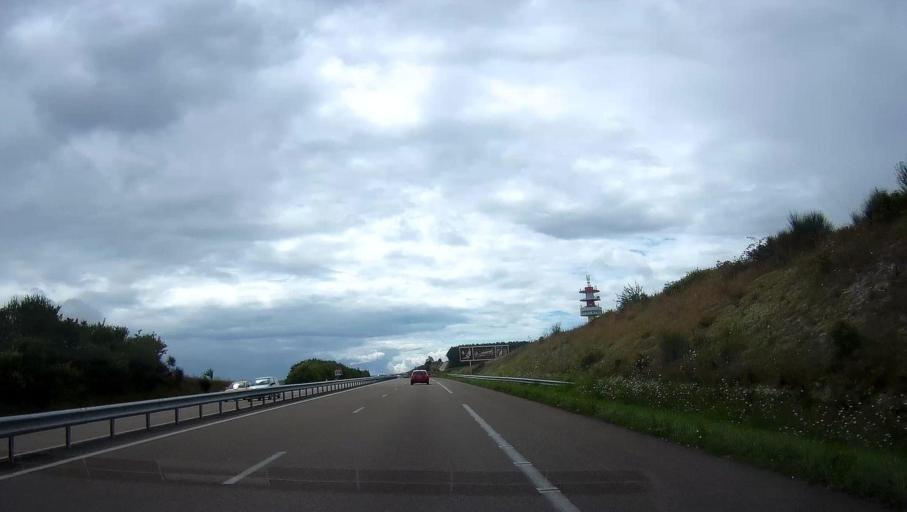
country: FR
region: Champagne-Ardenne
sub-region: Departement de l'Aube
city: Creney-pres-Troyes
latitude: 48.3731
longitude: 4.1579
